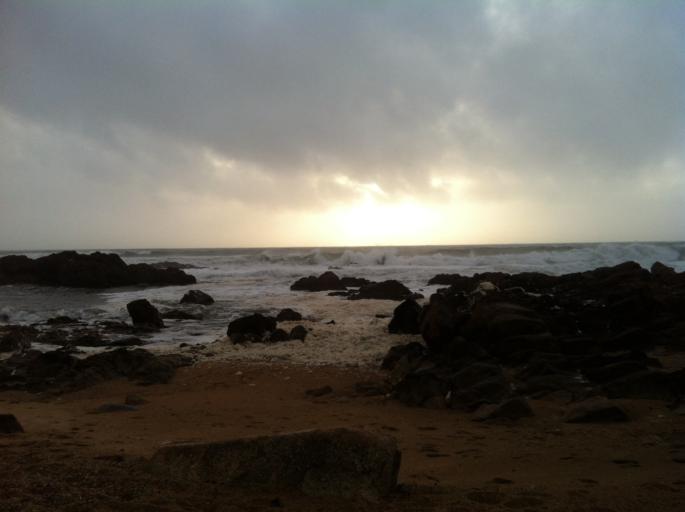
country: PT
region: Porto
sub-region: Matosinhos
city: Matosinhos
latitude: 41.1678
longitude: -8.6900
